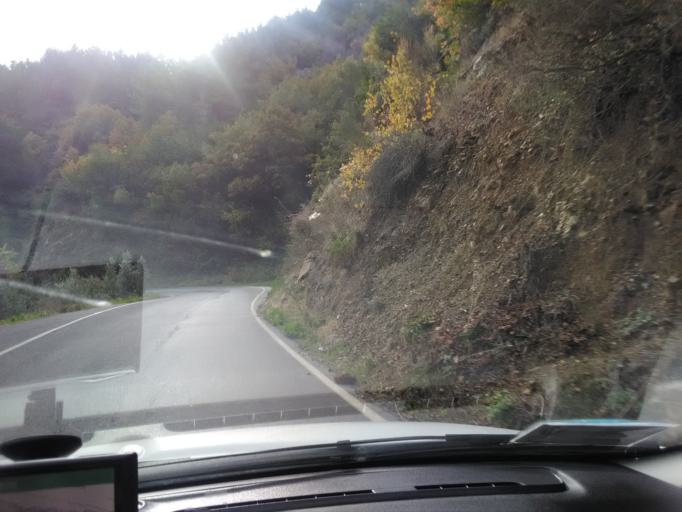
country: TR
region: Antalya
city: Gazipasa
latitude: 36.2534
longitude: 32.3967
